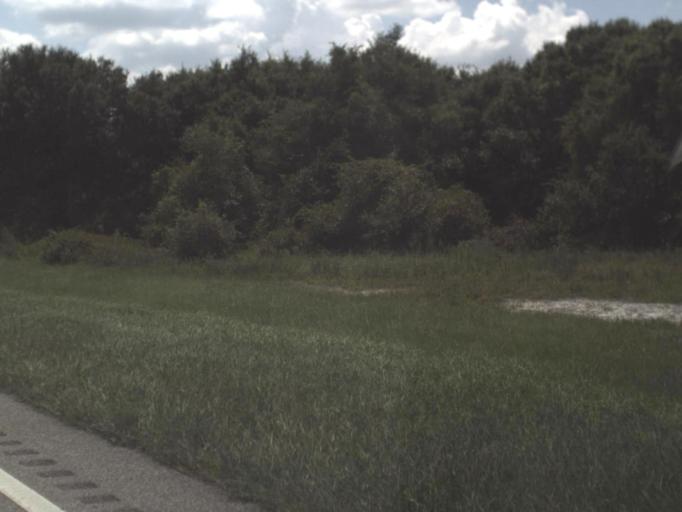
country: US
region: Florida
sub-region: Hillsborough County
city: Sun City Center
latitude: 27.6861
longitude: -82.3445
